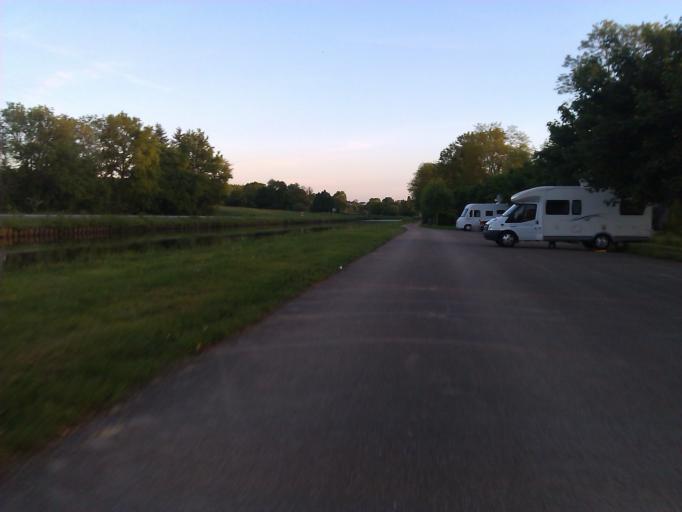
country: FR
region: Bourgogne
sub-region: Departement de Saone-et-Loire
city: Paray-le-Monial
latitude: 46.4498
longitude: 4.1567
